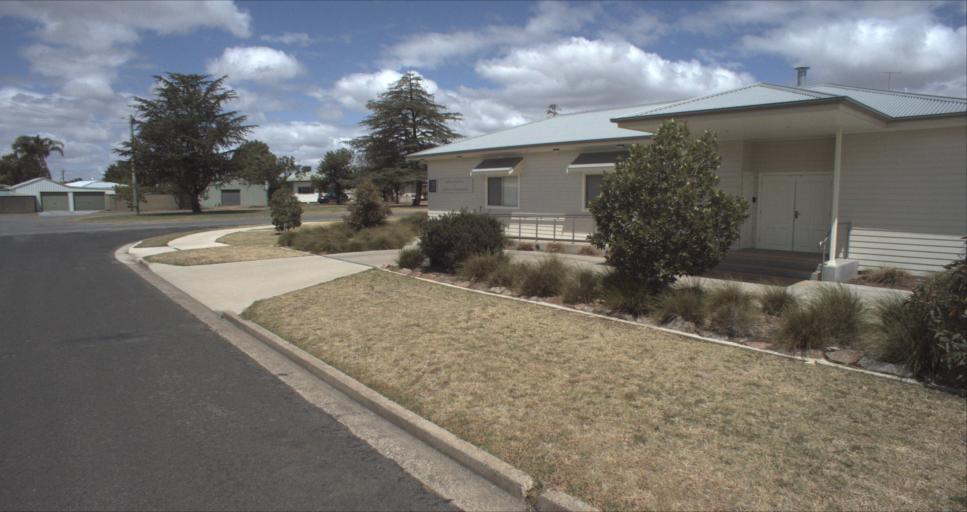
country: AU
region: New South Wales
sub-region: Leeton
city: Leeton
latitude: -34.5591
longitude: 146.3976
